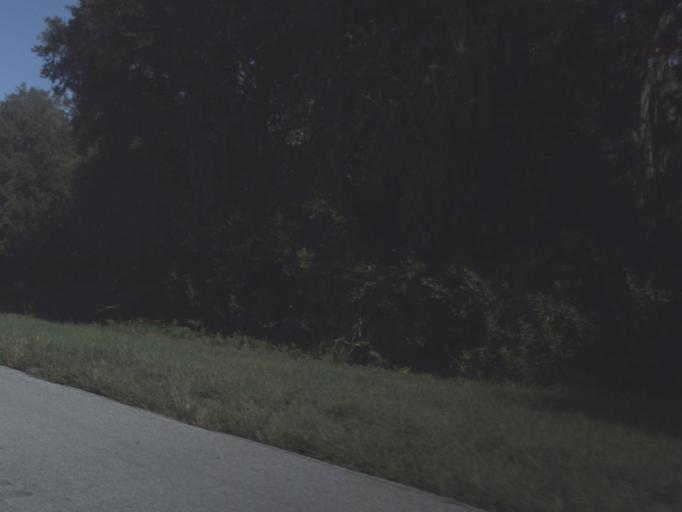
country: US
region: Florida
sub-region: Lake County
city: Leesburg
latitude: 28.7775
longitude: -81.9654
